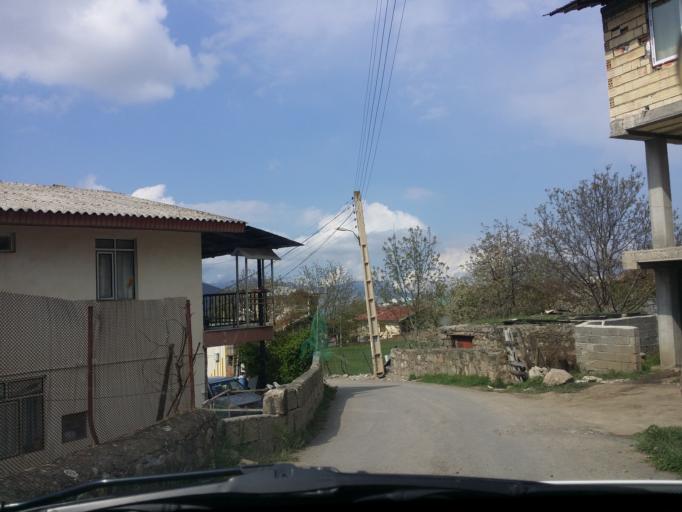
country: IR
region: Mazandaran
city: `Abbasabad
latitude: 36.4848
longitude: 51.1373
